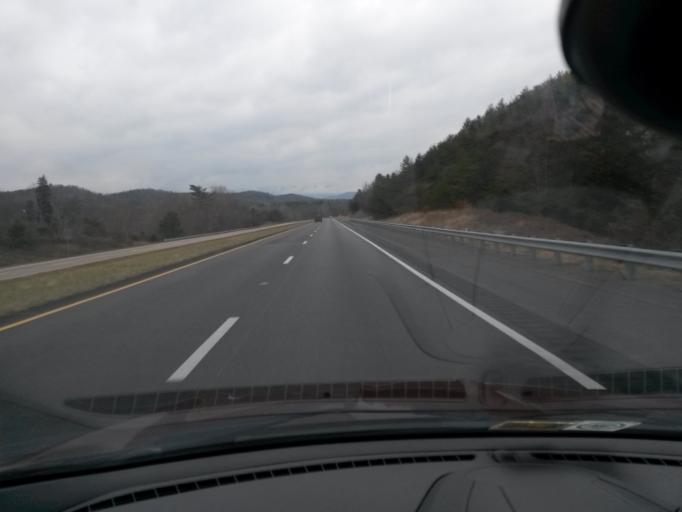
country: US
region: Virginia
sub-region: Alleghany County
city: Clifton Forge
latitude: 37.8025
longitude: -79.7350
